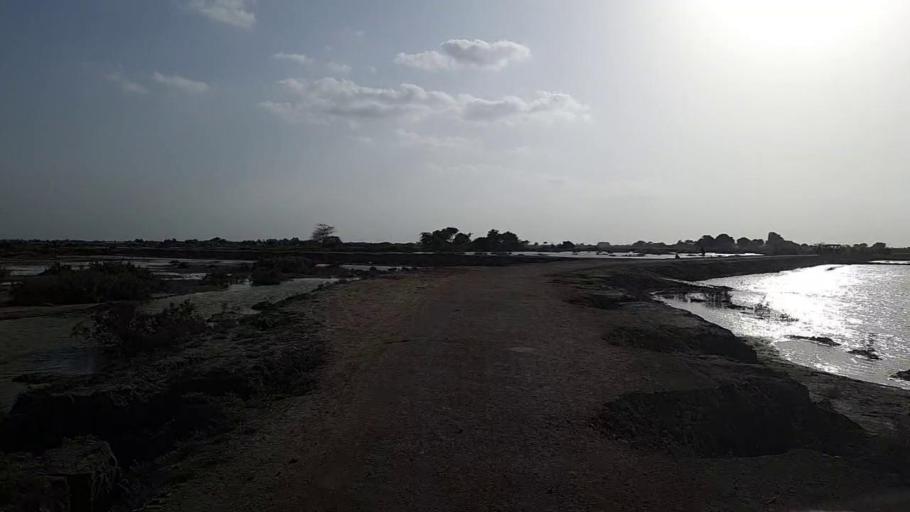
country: PK
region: Sindh
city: Kario
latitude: 24.6708
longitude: 68.4629
